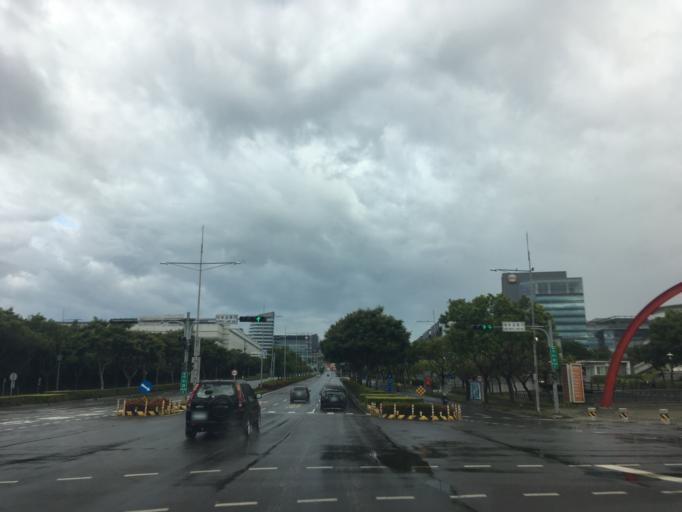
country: TW
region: Taiwan
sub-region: Taichung City
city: Taichung
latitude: 24.2083
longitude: 120.6194
